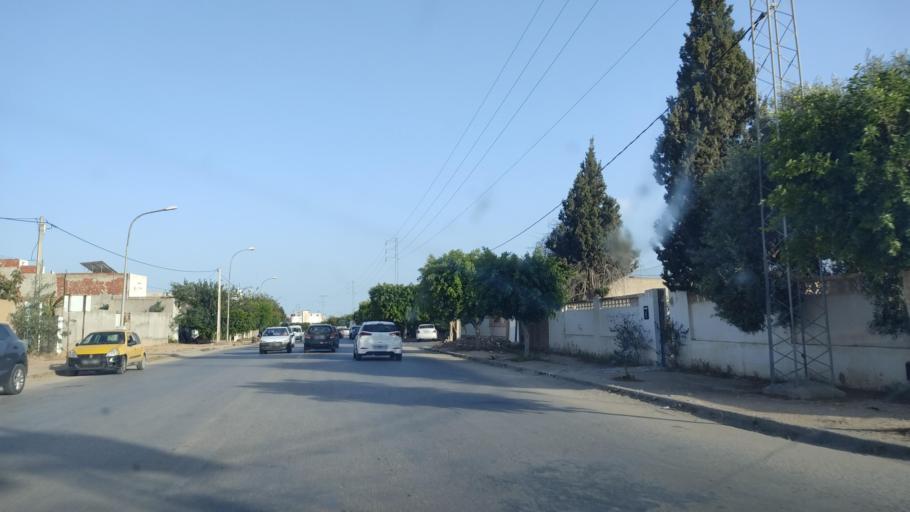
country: TN
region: Safaqis
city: Sfax
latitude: 34.7878
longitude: 10.6898
